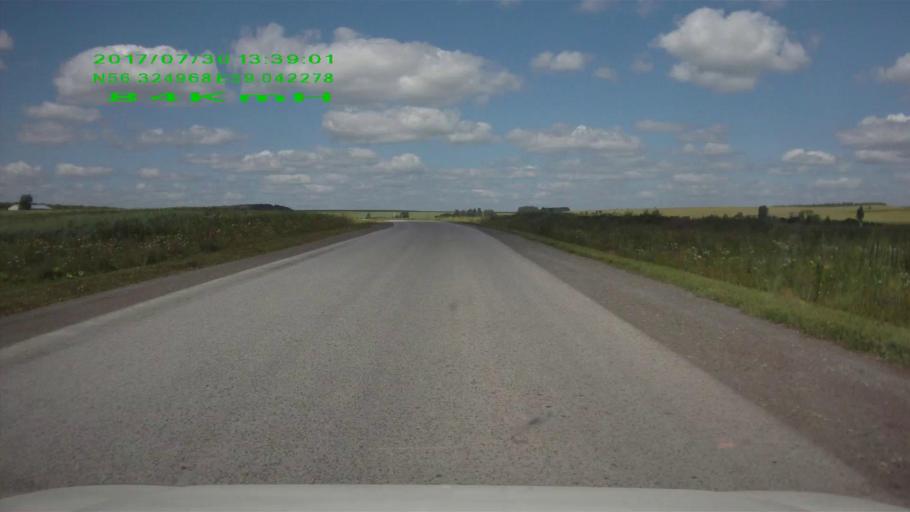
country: RU
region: Sverdlovsk
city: Mikhaylovsk
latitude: 56.3251
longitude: 59.0424
